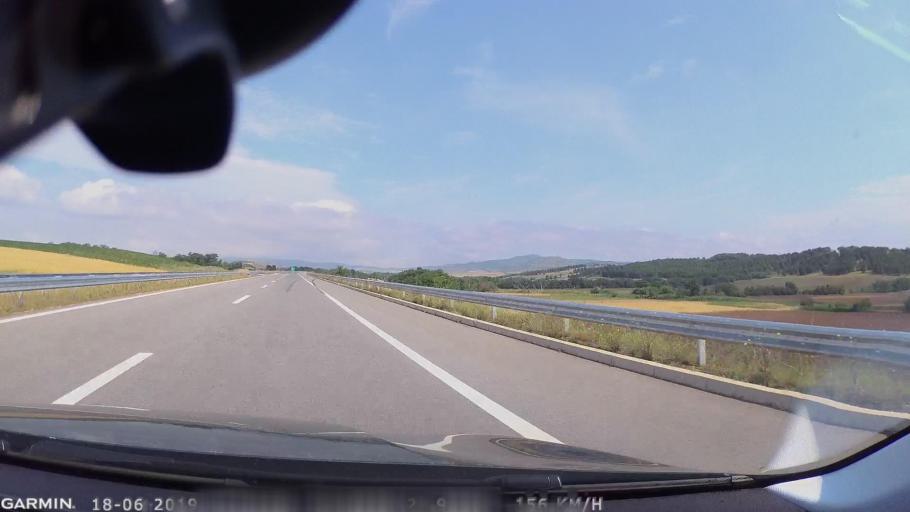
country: MK
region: Sveti Nikole
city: Gorobinci
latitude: 41.9067
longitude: 21.9070
